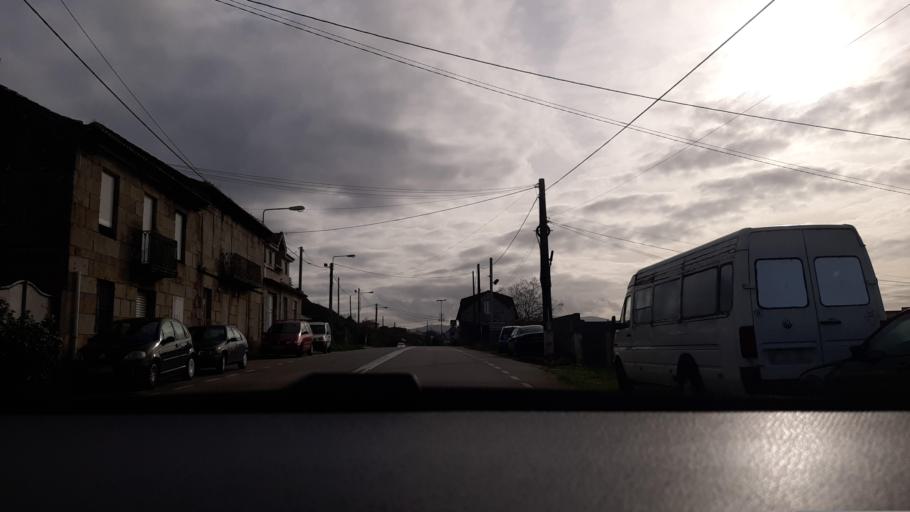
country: ES
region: Galicia
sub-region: Provincia de Pontevedra
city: Nigran
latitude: 42.1684
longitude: -8.8012
